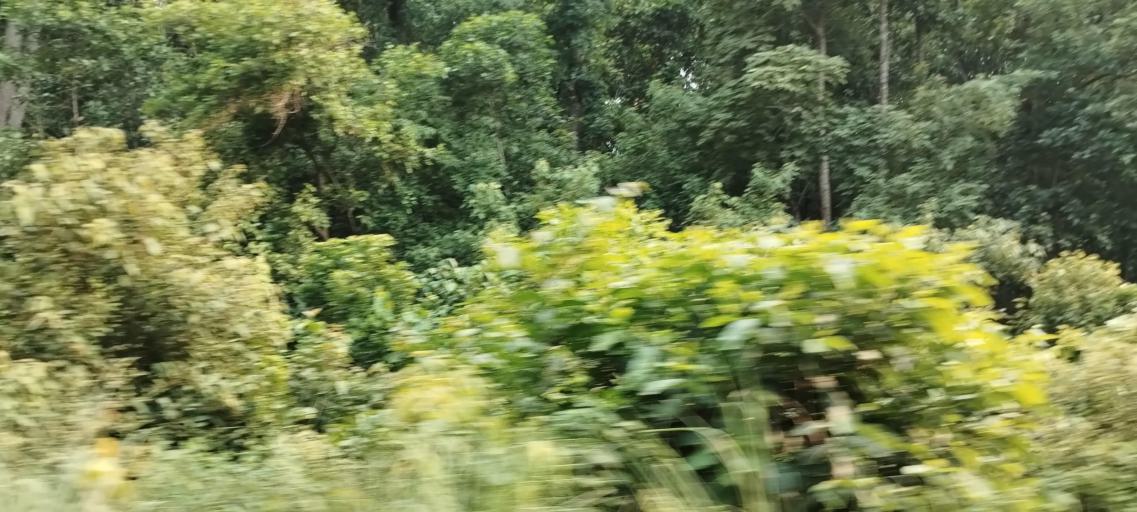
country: NP
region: Mid Western
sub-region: Bheri Zone
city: Bardiya
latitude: 28.4307
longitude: 81.3581
